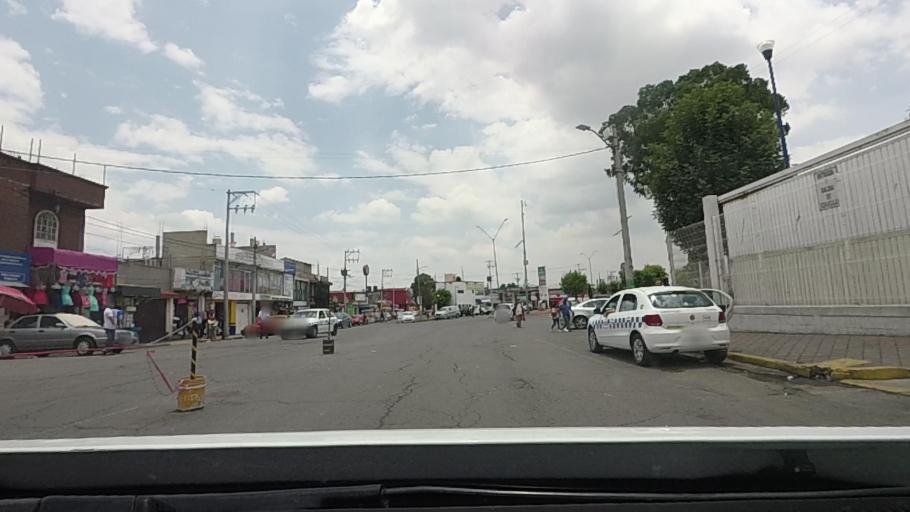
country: MX
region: Mexico
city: Chalco de Diaz Covarrubias
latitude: 19.2623
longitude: -98.8994
